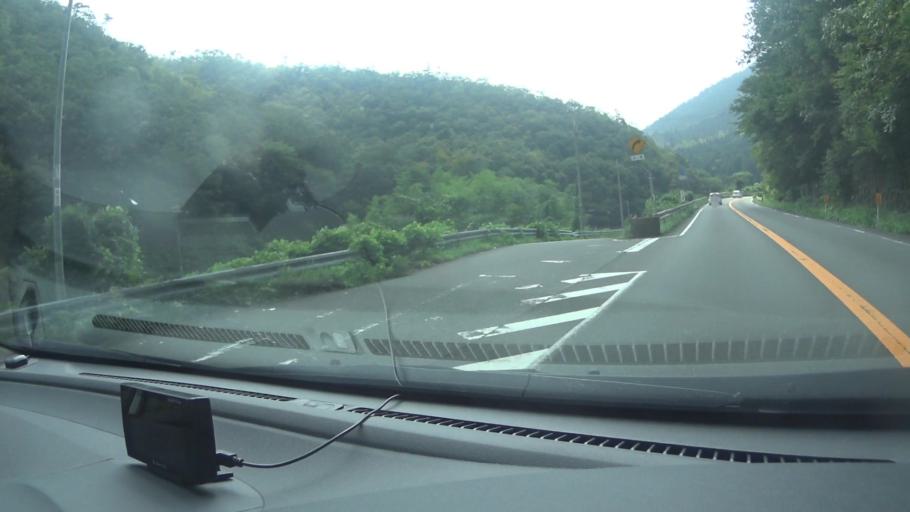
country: JP
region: Hyogo
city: Sasayama
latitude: 35.1473
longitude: 135.3545
